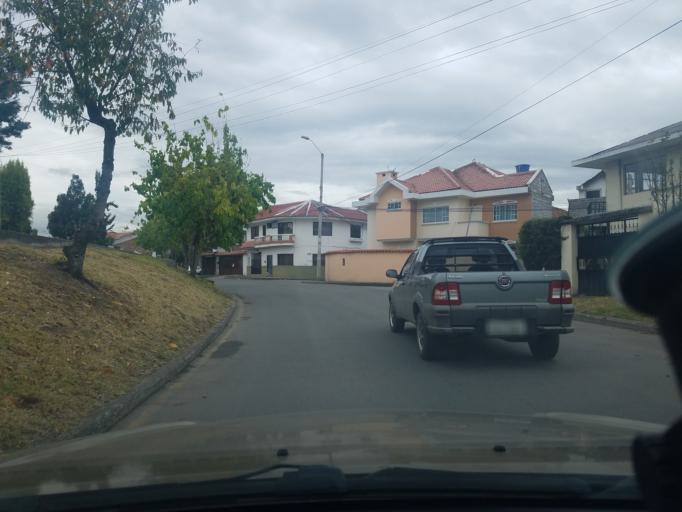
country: EC
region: Azuay
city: Cuenca
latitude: -2.9033
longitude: -78.9821
